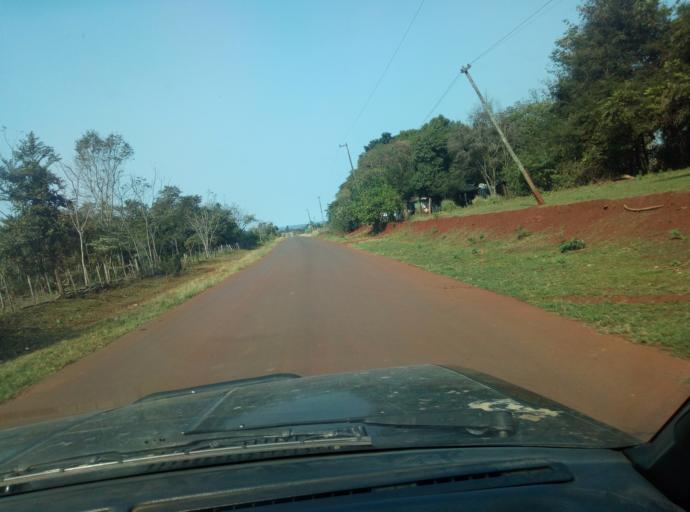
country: PY
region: Caaguazu
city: Carayao
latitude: -25.2196
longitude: -56.2889
